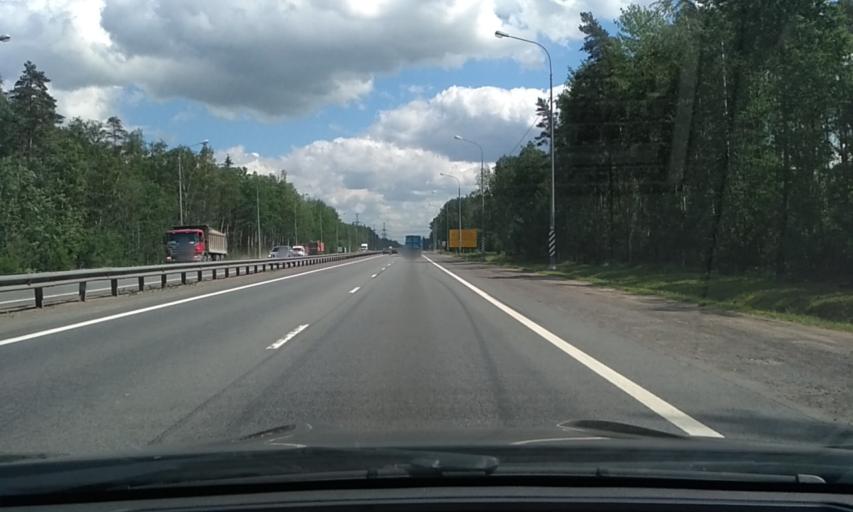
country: RU
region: Leningrad
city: Rybatskoye
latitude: 59.8923
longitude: 30.5428
